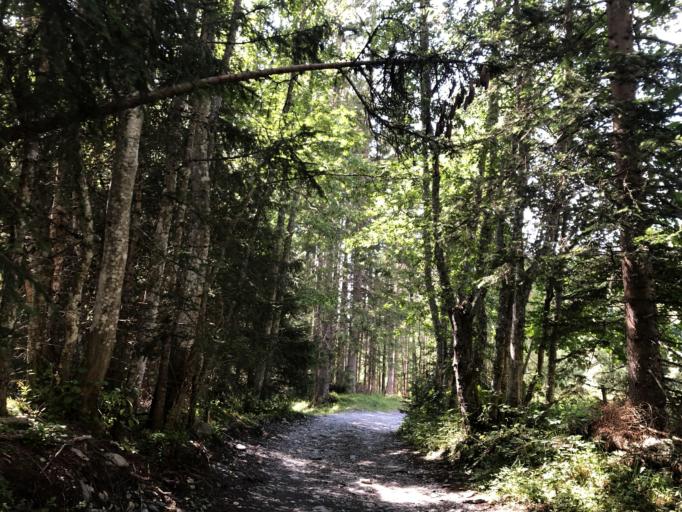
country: FR
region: Rhone-Alpes
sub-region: Departement de la Haute-Savoie
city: Megeve
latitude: 45.8305
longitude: 6.6617
